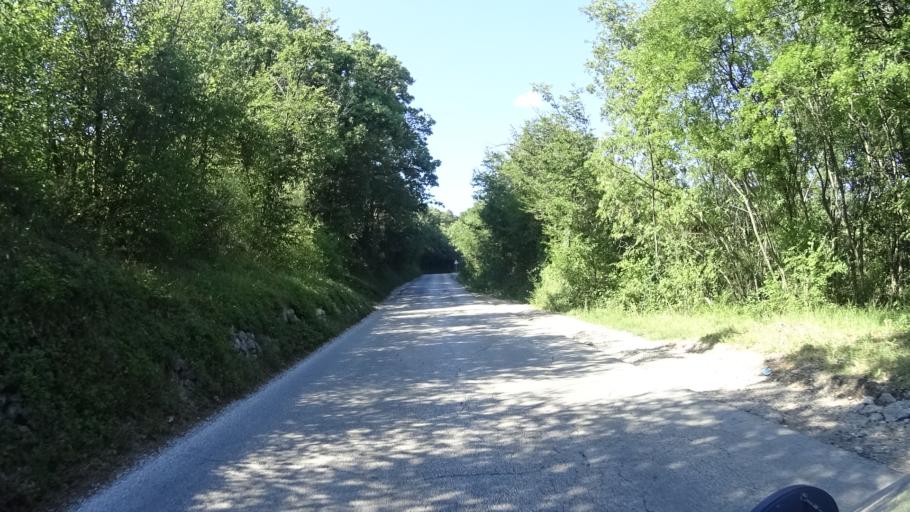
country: HR
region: Istarska
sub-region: Grad Labin
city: Labin
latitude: 45.0694
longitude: 14.1191
